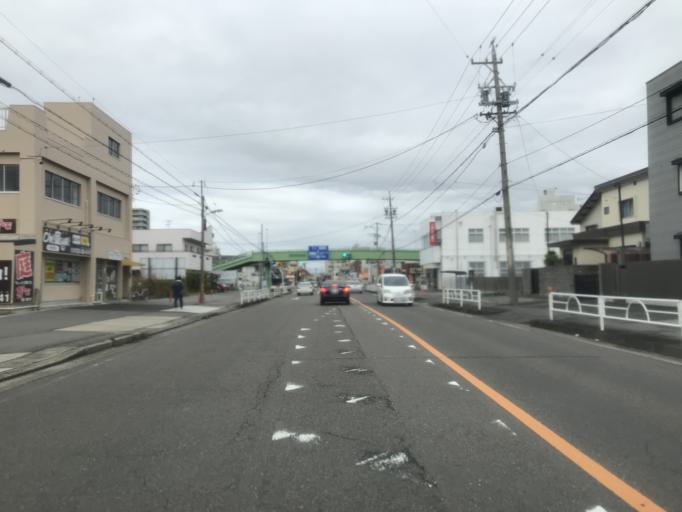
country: JP
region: Aichi
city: Nagoya-shi
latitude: 35.1976
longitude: 136.8646
